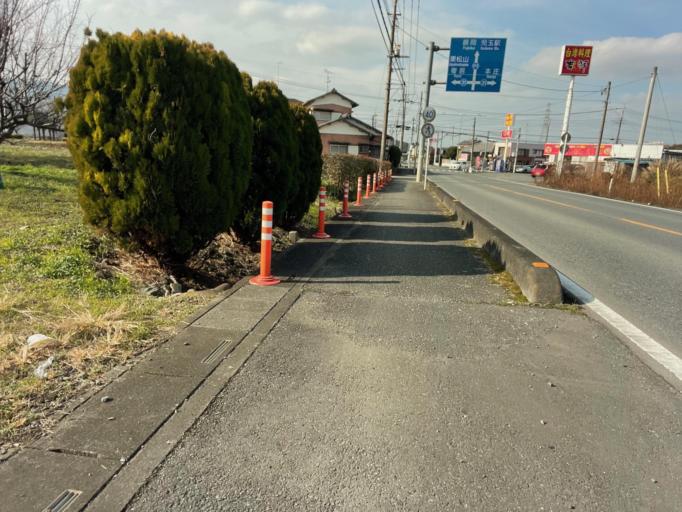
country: JP
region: Saitama
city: Yorii
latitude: 36.1575
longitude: 139.1872
